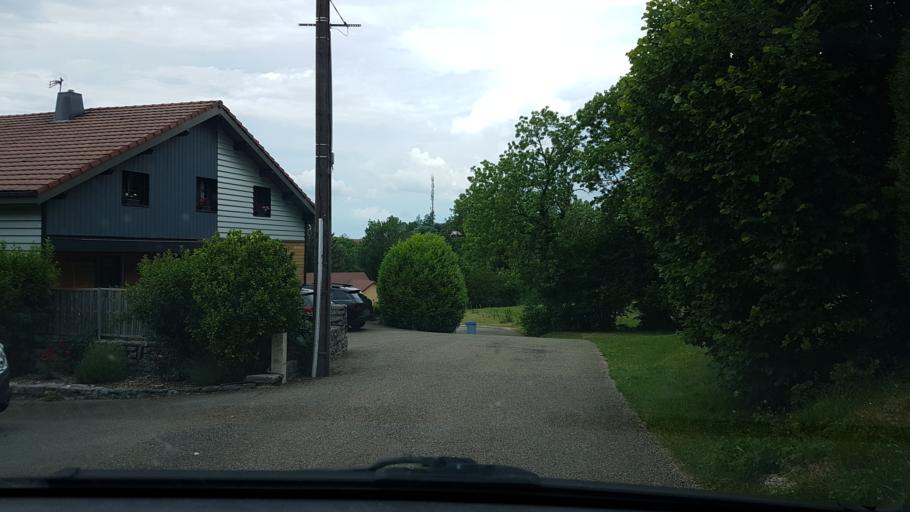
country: FR
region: Franche-Comte
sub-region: Departement du Jura
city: Clairvaux-les-Lacs
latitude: 46.5651
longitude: 5.7595
